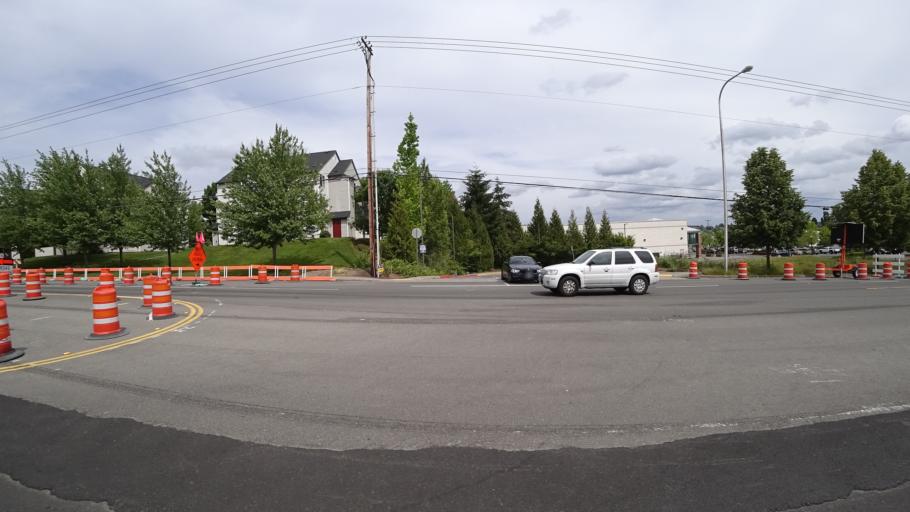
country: US
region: Oregon
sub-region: Washington County
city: Bethany
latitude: 45.5595
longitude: -122.8677
